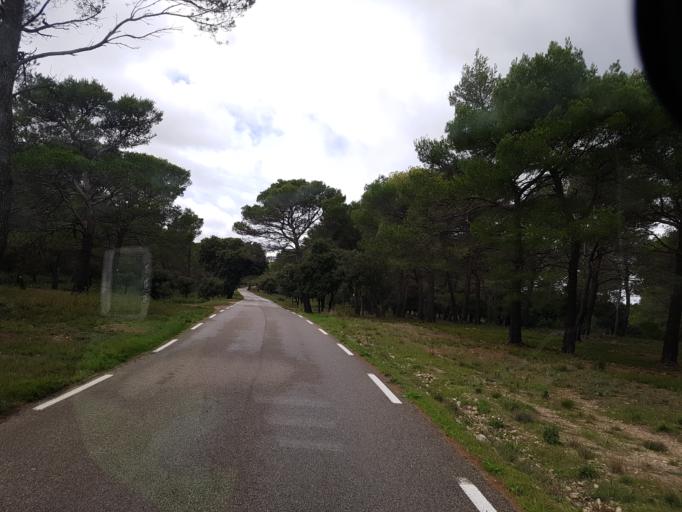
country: FR
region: Provence-Alpes-Cote d'Azur
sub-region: Departement des Bouches-du-Rhone
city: Cuges-les-Pins
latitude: 43.2537
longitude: 5.7420
